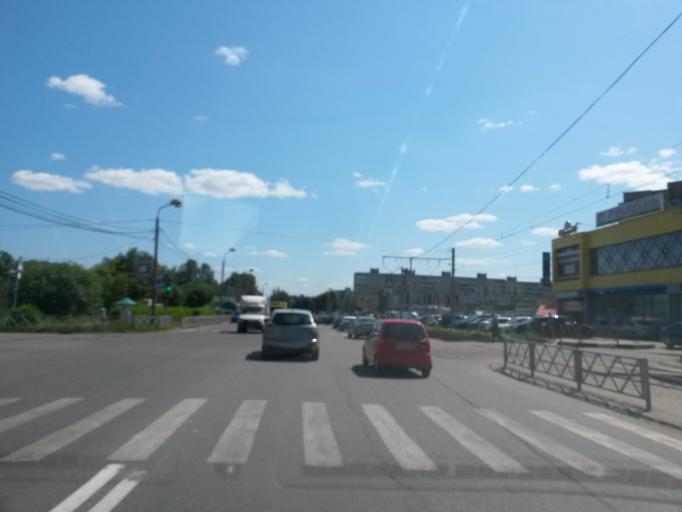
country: RU
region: Jaroslavl
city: Yaroslavl
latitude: 57.6863
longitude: 39.7658
